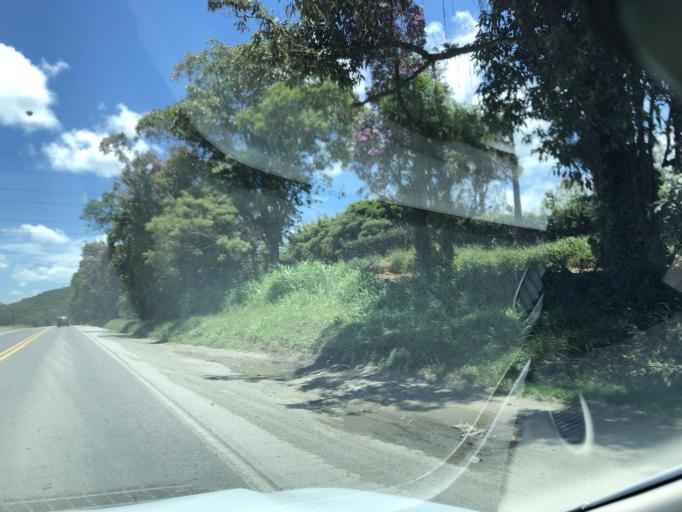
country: BR
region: Santa Catarina
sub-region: Joinville
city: Joinville
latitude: -26.4293
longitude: -48.7947
